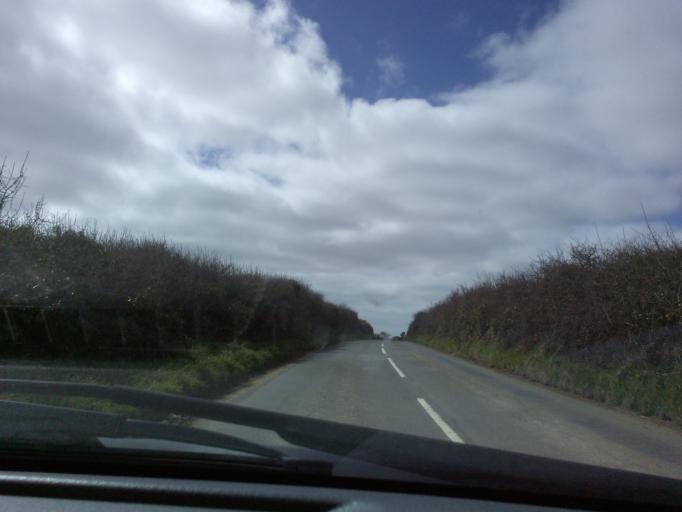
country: GB
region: England
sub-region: Cornwall
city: St. Buryan
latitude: 50.0630
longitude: -5.5961
